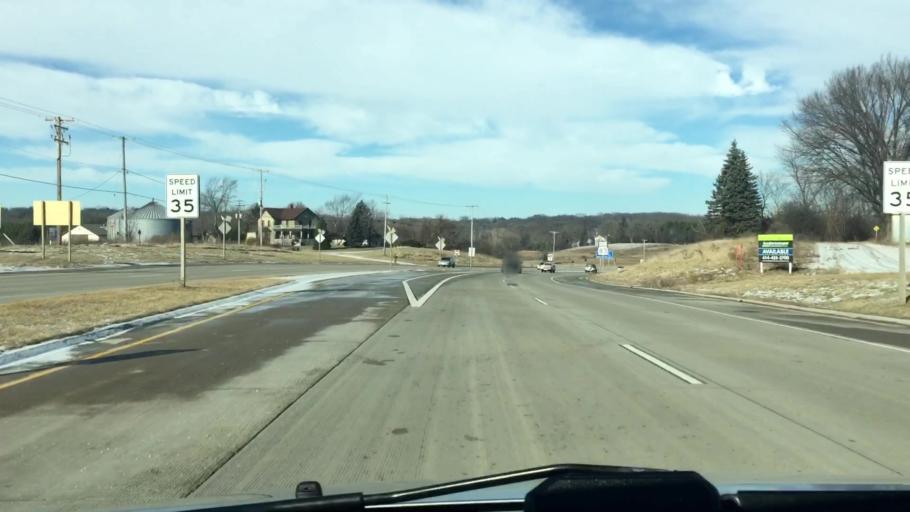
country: US
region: Wisconsin
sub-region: Waukesha County
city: Mukwonago
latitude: 42.8813
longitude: -88.3420
